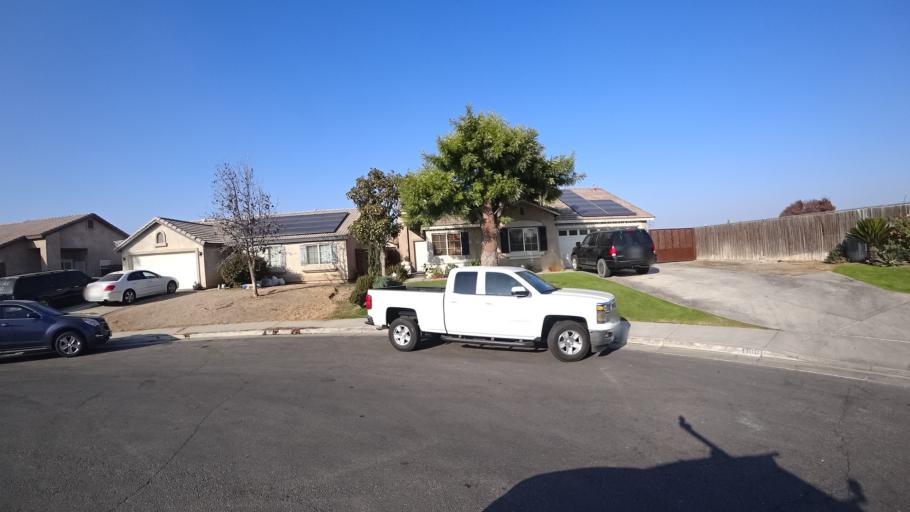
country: US
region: California
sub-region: Kern County
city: Greenfield
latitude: 35.2819
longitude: -119.0143
